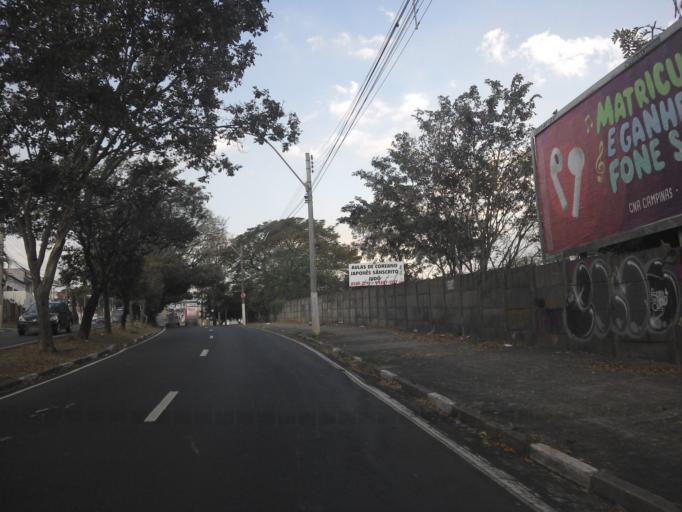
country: BR
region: Sao Paulo
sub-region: Campinas
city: Campinas
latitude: -22.8941
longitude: -47.0875
